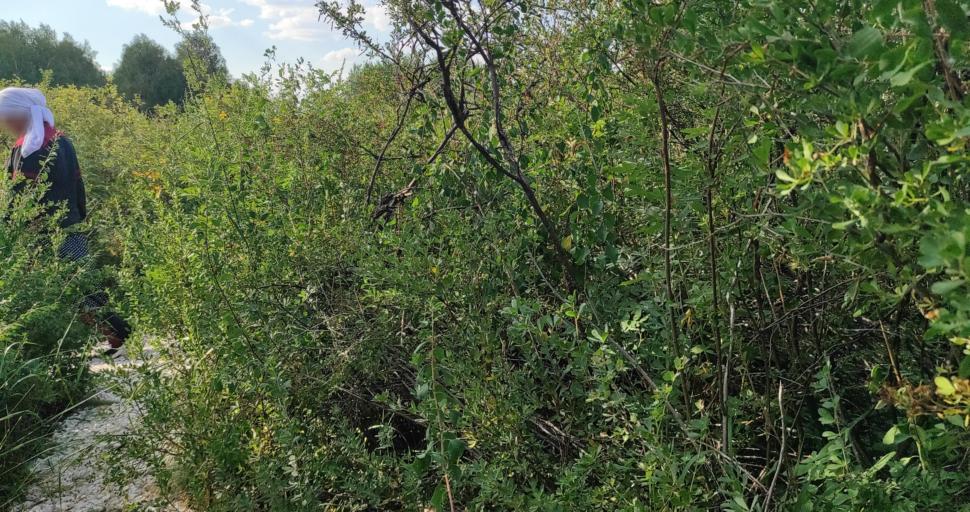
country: RU
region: Bashkortostan
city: Baymak
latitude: 52.5246
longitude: 58.4890
